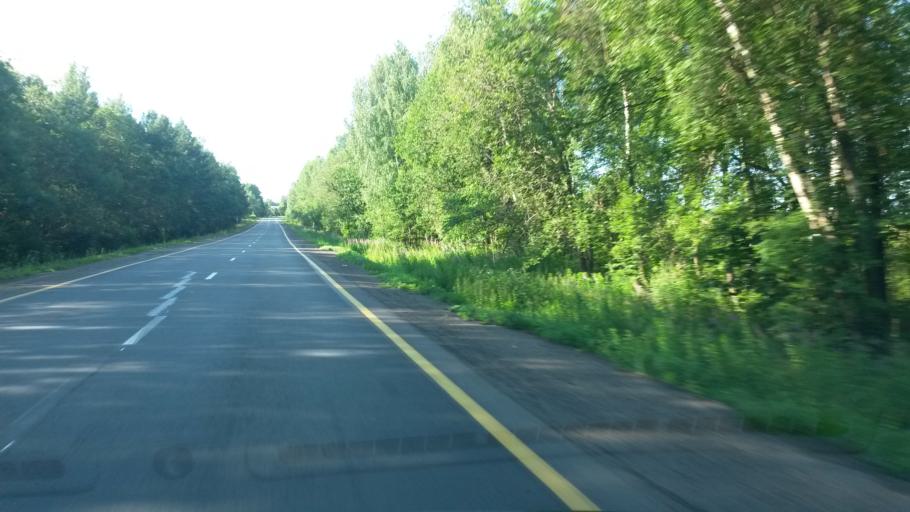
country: RU
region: Jaroslavl
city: Gavrilov-Yam
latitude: 57.2870
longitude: 39.9530
